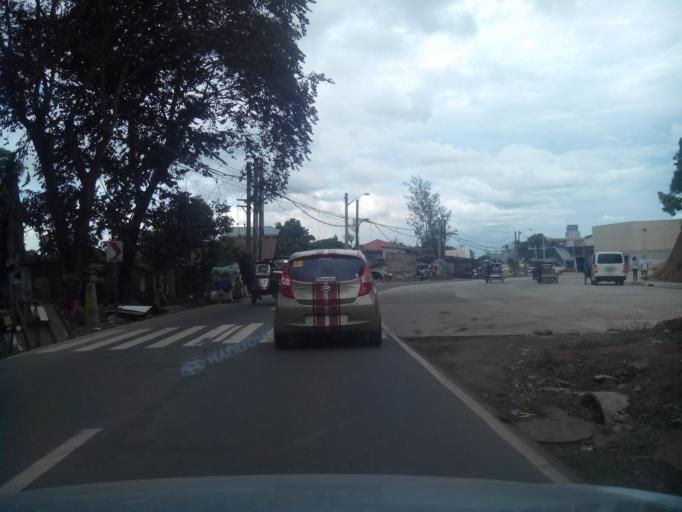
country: PH
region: Calabarzon
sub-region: Province of Rizal
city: Teresa
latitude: 14.5937
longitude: 121.1757
